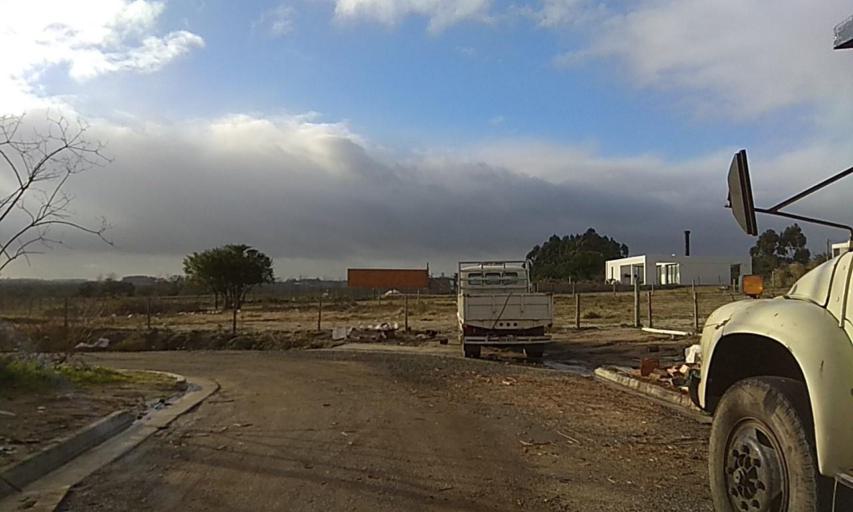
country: UY
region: Florida
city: Florida
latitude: -34.0850
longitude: -56.2100
